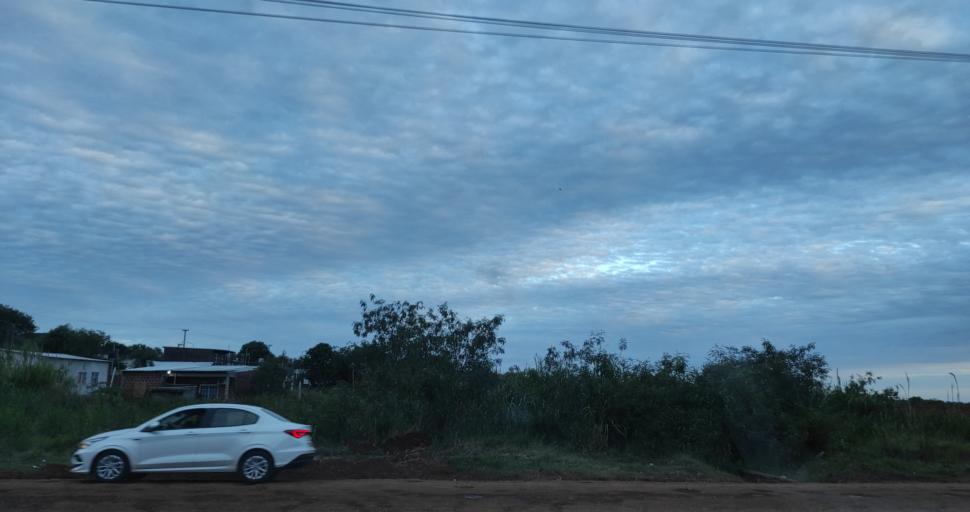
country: AR
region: Misiones
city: Garupa
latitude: -27.4718
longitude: -55.8456
